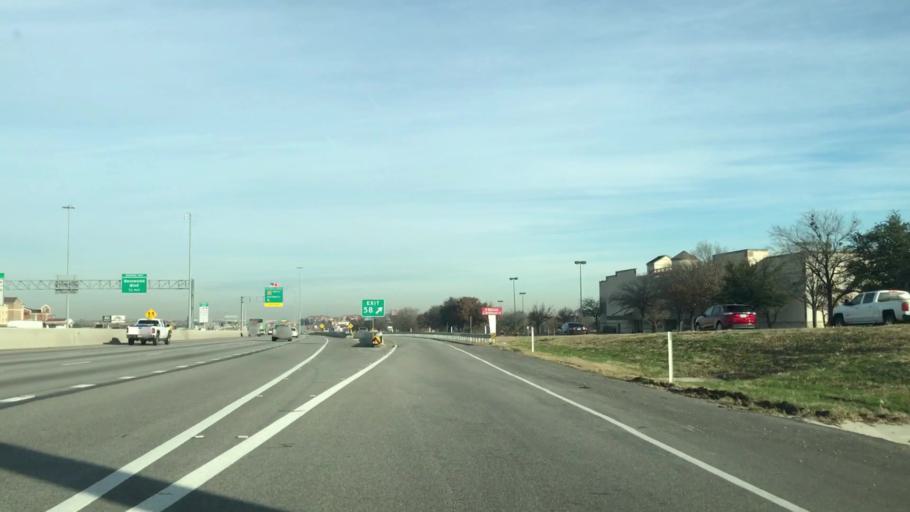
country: US
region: Texas
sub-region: Tarrant County
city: Blue Mound
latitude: 32.8528
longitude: -97.3125
